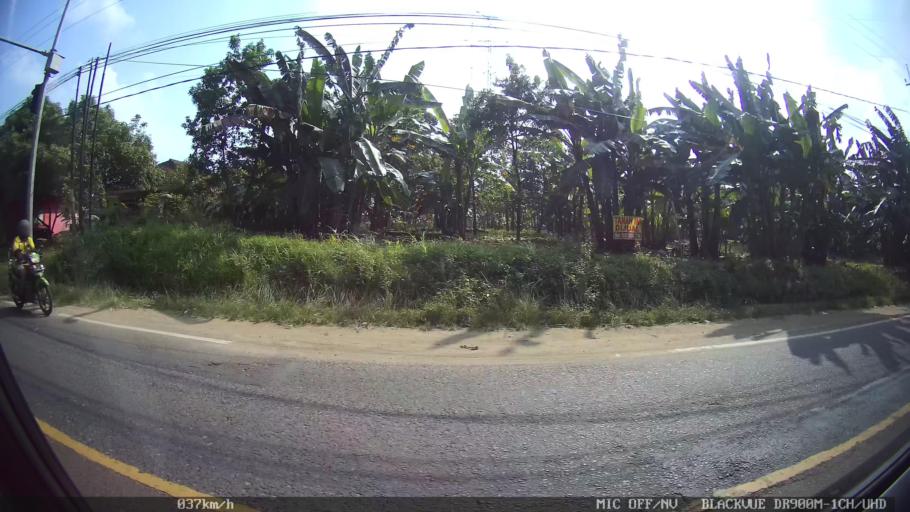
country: ID
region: Lampung
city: Kedaton
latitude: -5.3865
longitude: 105.2022
